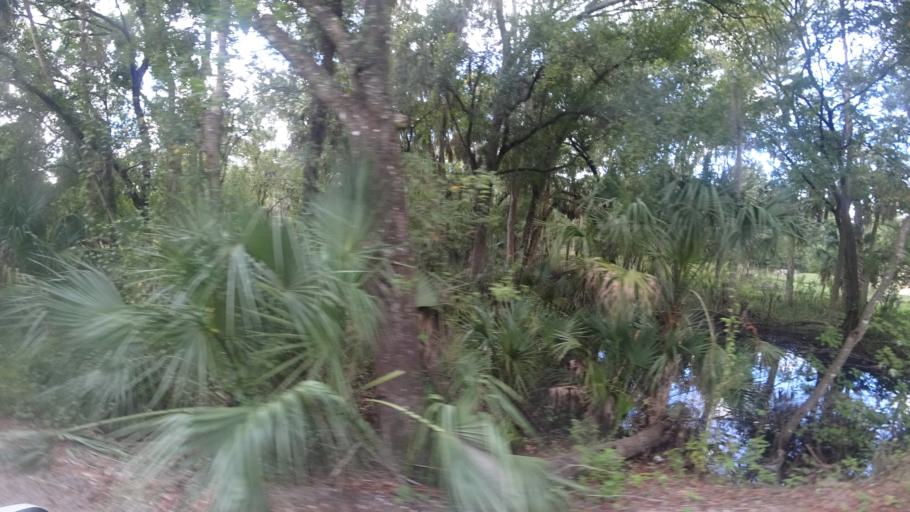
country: US
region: Florida
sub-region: Hillsborough County
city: Sun City Center
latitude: 27.6477
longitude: -82.3756
